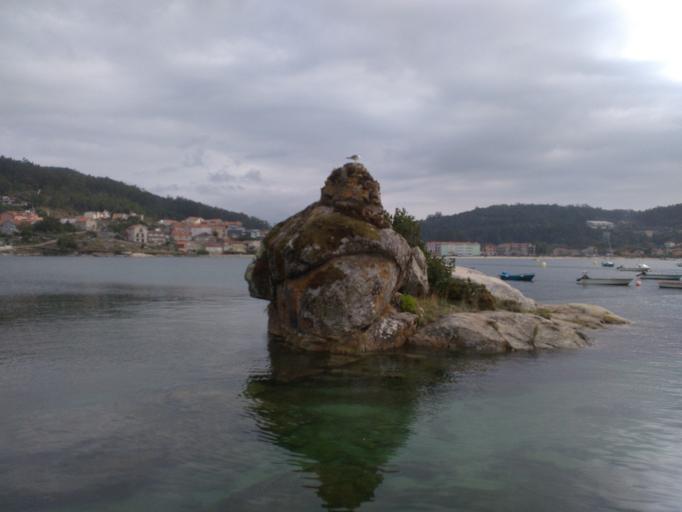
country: ES
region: Galicia
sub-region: Provincia de Pontevedra
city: Cangas
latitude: 42.2799
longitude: -8.8202
